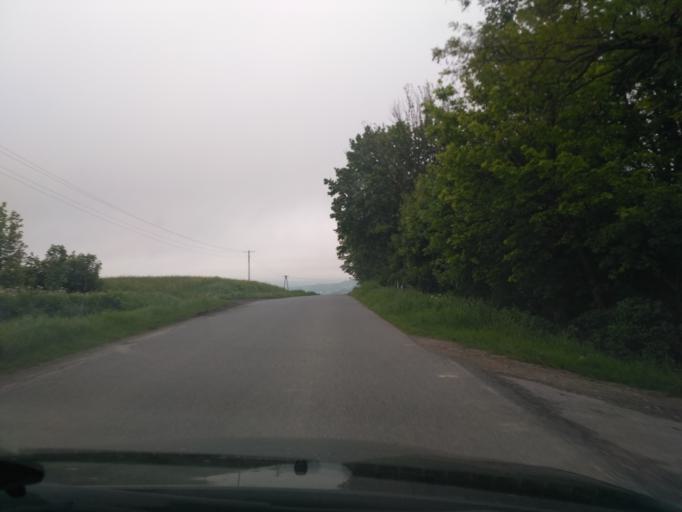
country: PL
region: Subcarpathian Voivodeship
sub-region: Powiat ropczycko-sedziszowski
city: Niedzwiada
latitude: 49.9675
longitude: 21.4886
